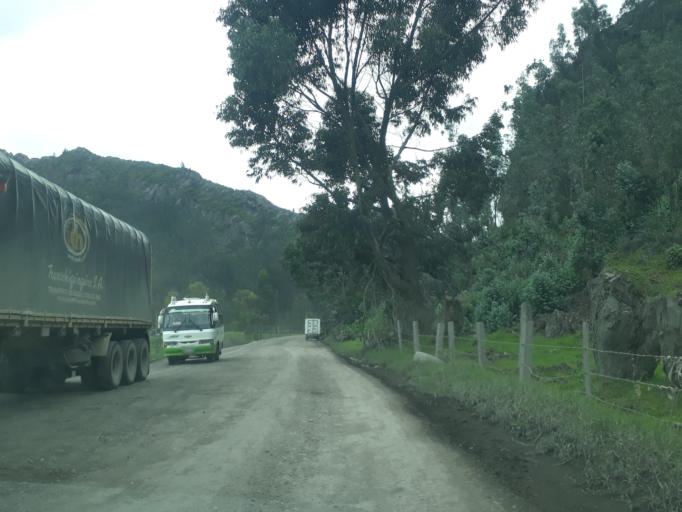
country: CO
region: Cundinamarca
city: Lenguazaque
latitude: 5.3280
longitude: -73.7028
